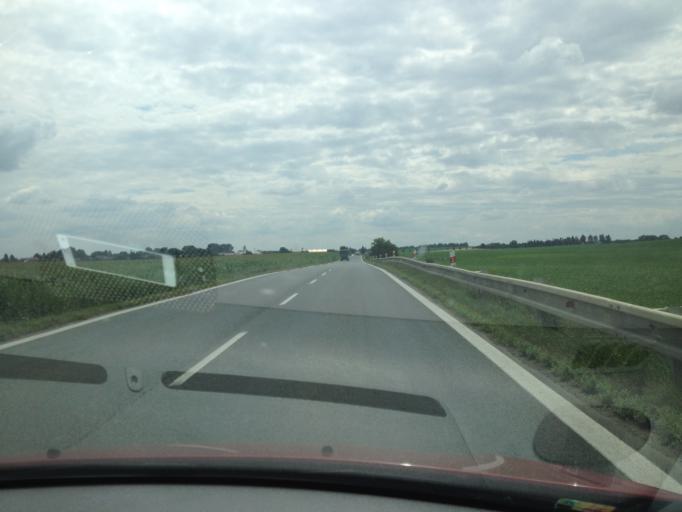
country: CZ
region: Olomoucky
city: Litovel
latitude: 49.6837
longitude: 17.0821
